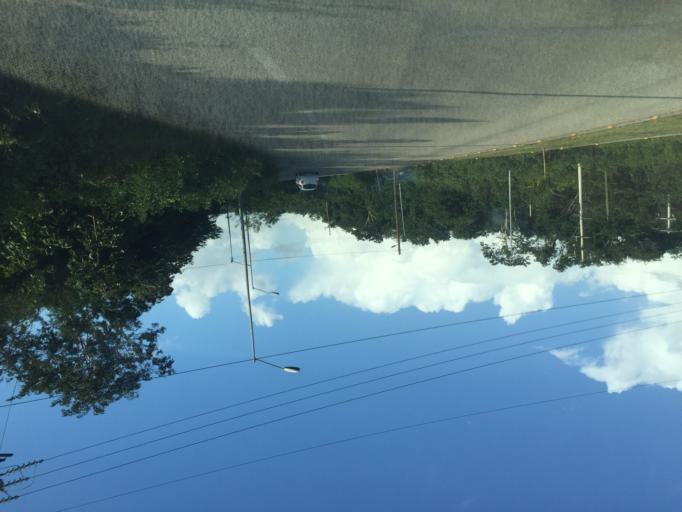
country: MX
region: Quintana Roo
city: Coba
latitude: 20.5073
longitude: -87.7179
